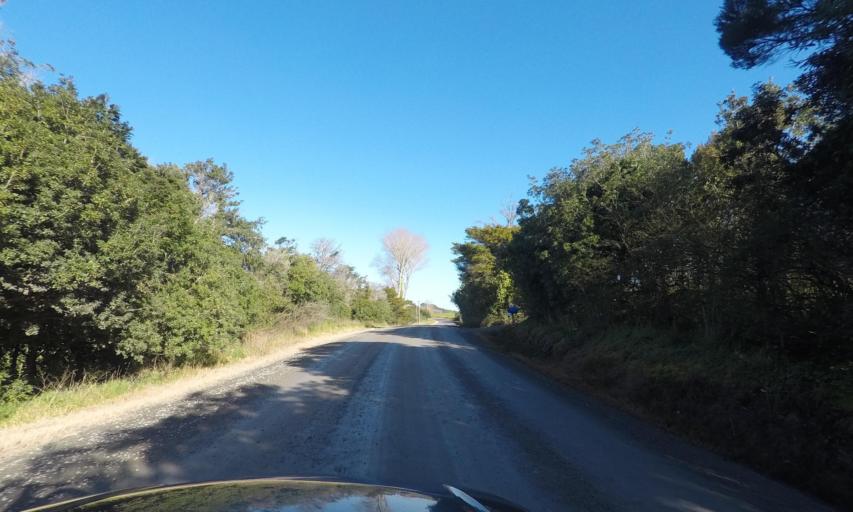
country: NZ
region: Auckland
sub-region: Auckland
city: Wellsford
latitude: -36.1526
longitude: 174.6040
